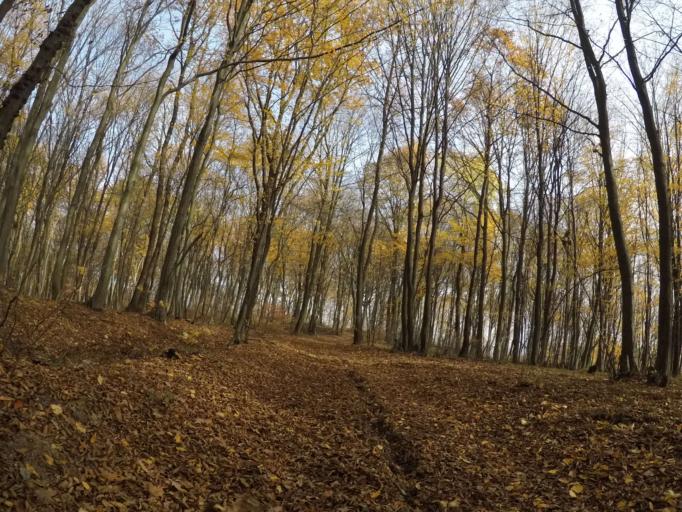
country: SK
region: Presovsky
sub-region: Okres Presov
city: Presov
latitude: 48.9288
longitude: 21.2205
